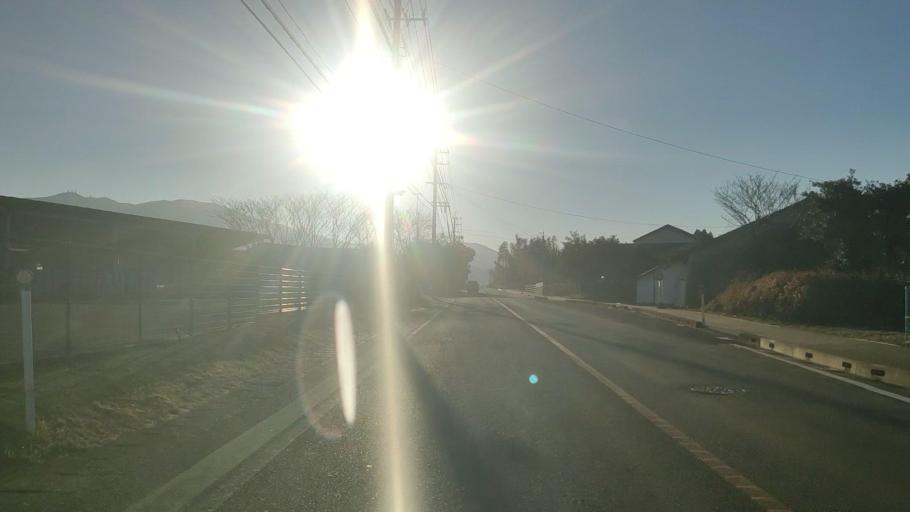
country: JP
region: Miyazaki
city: Miyazaki-shi
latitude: 31.8356
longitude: 131.3251
